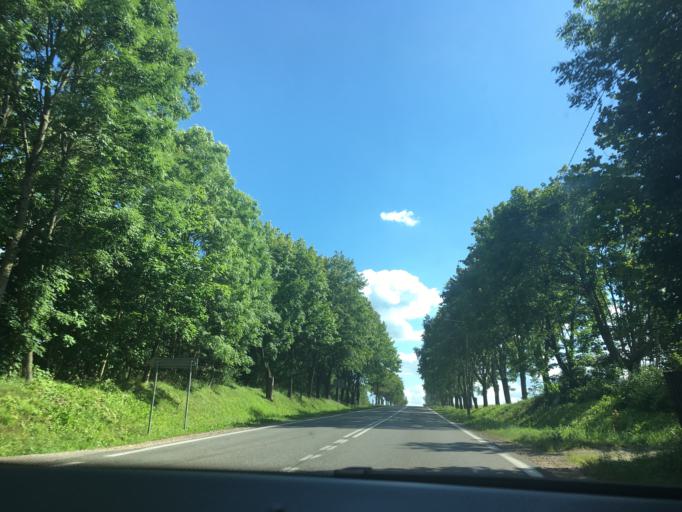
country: PL
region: Podlasie
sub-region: Powiat sokolski
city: Janow
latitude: 53.3932
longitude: 23.1140
